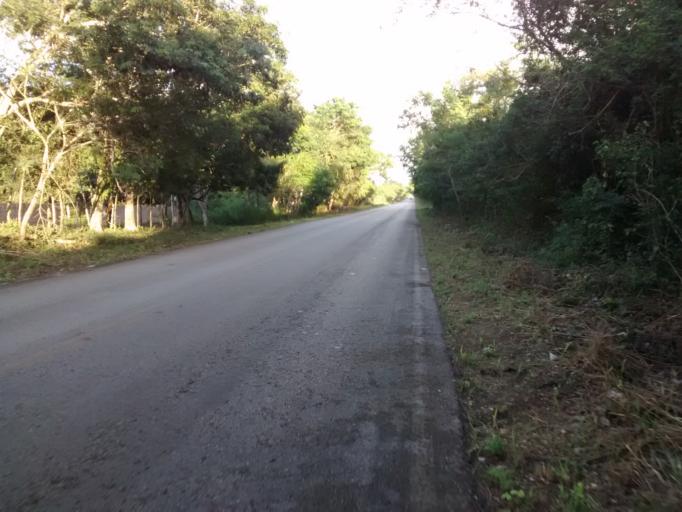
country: MX
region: Yucatan
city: Valladolid
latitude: 20.7311
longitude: -88.2169
